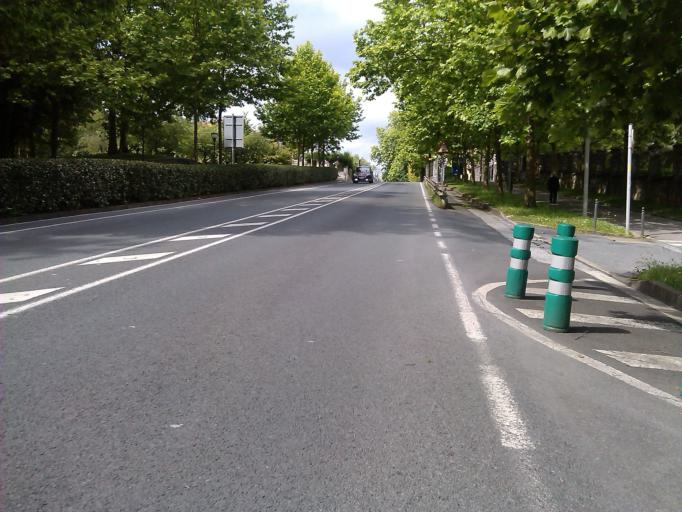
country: ES
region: Basque Country
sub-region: Provincia de Guipuzcoa
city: Irun
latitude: 43.3350
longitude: -1.7997
